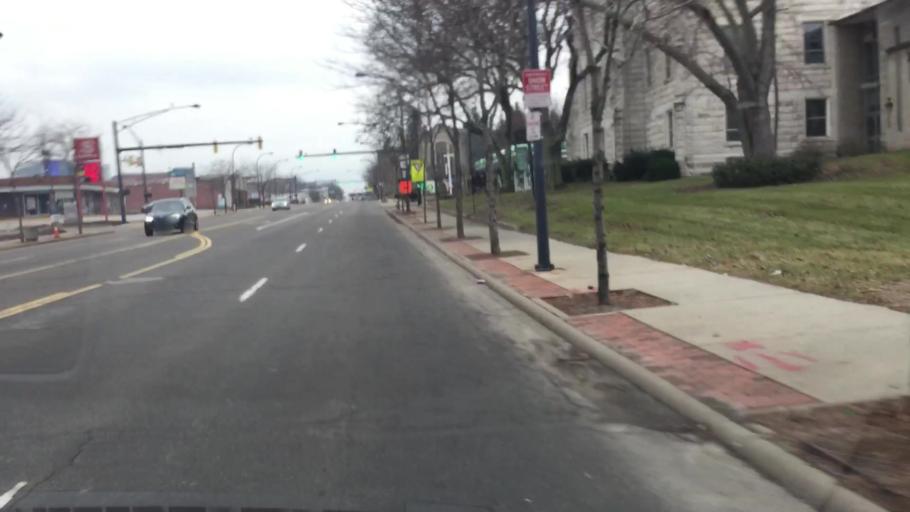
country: US
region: Ohio
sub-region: Summit County
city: Akron
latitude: 41.0820
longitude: -81.5089
